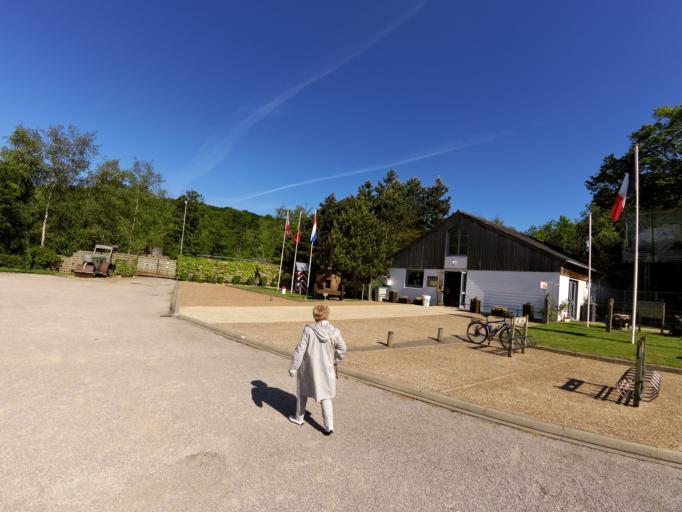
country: FR
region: Nord-Pas-de-Calais
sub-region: Departement du Nord
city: Watten
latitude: 50.8270
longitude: 2.1824
